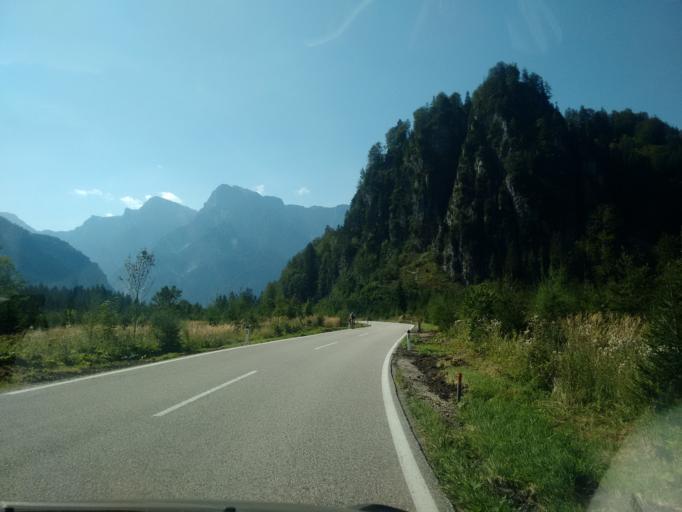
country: AT
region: Upper Austria
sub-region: Politischer Bezirk Gmunden
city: Gruenau im Almtal
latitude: 47.7623
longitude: 13.9542
